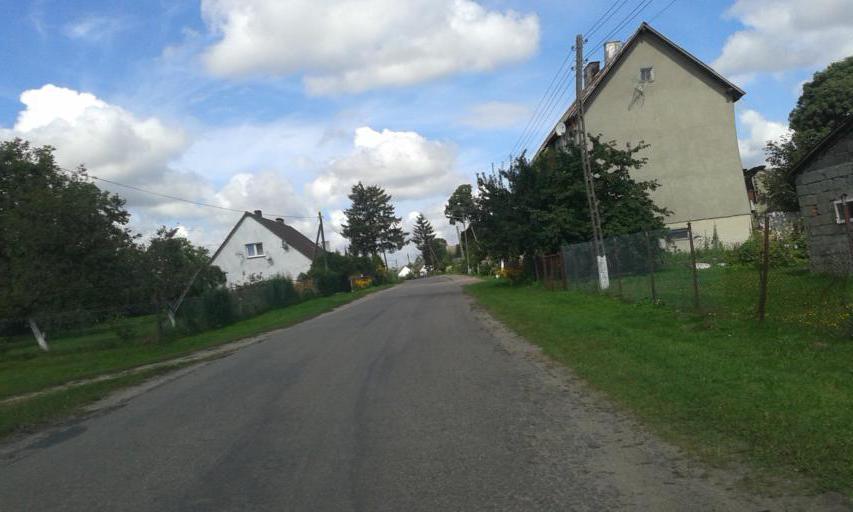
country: PL
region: West Pomeranian Voivodeship
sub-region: Powiat slawienski
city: Slawno
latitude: 54.3022
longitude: 16.6283
